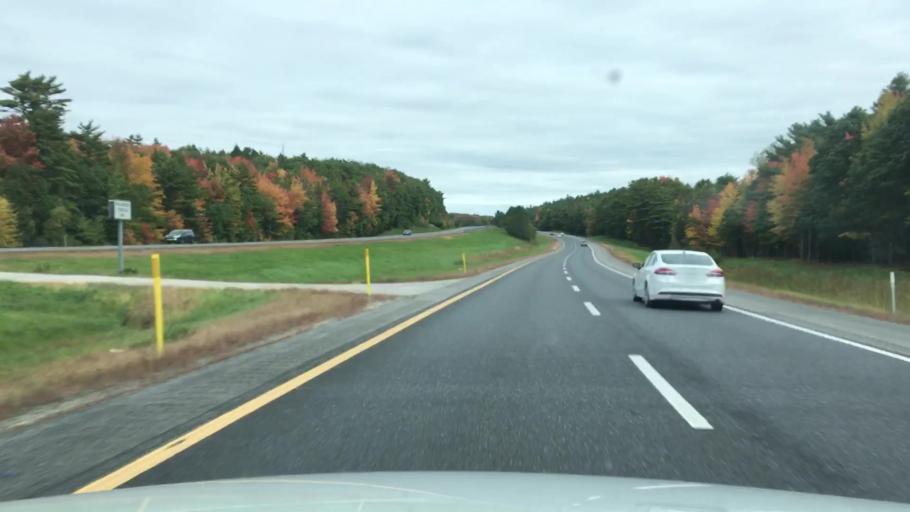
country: US
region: Maine
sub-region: Sagadahoc County
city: Topsham
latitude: 43.9821
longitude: -69.9436
